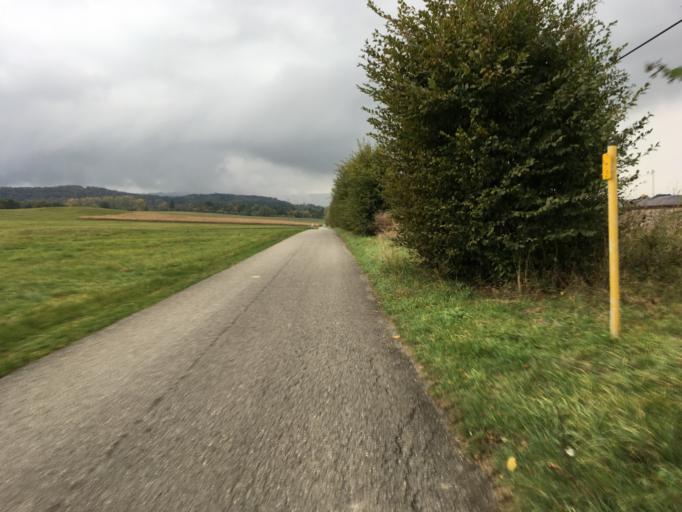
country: DE
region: Baden-Wuerttemberg
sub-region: Tuebingen Region
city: Nehren
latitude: 48.4379
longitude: 9.0829
